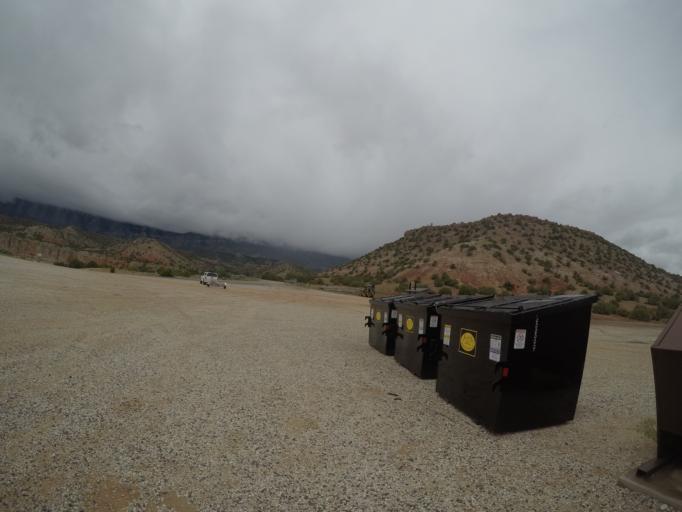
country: US
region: Wyoming
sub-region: Big Horn County
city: Lovell
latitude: 45.0959
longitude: -108.2098
